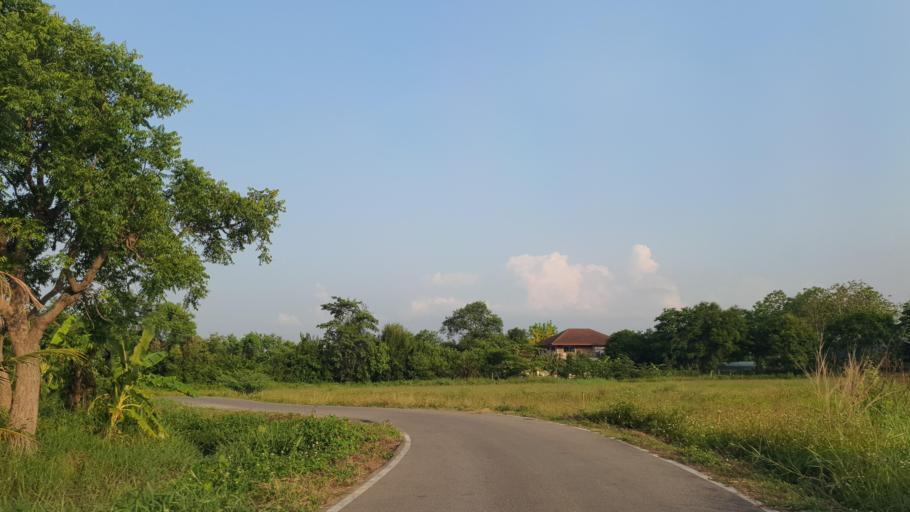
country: TH
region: Chiang Mai
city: San Pa Tong
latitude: 18.6390
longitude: 98.8750
